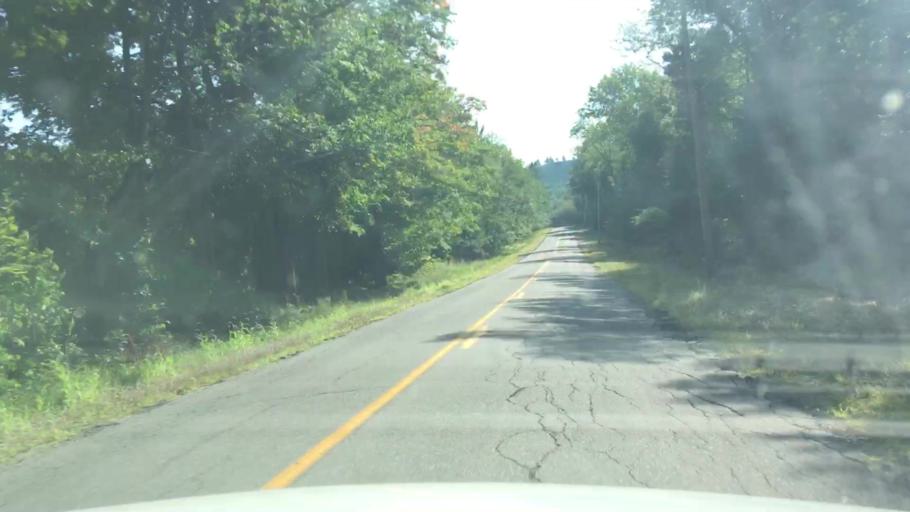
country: US
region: Maine
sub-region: Penobscot County
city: Enfield
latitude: 45.3005
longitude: -68.5504
